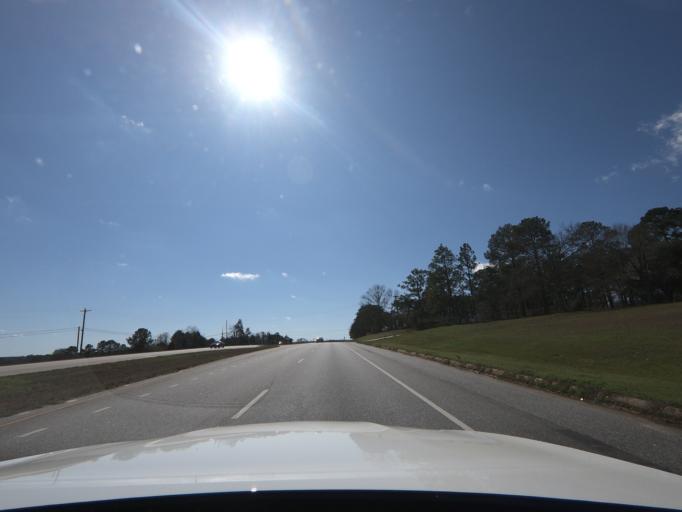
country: US
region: Alabama
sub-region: Barbour County
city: Eufaula
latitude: 31.7815
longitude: -85.1759
